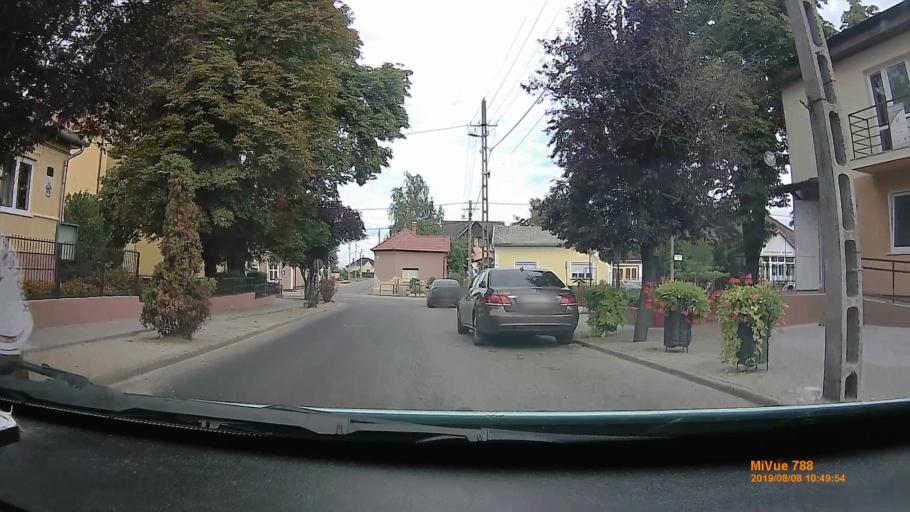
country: HU
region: Szabolcs-Szatmar-Bereg
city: Balkany
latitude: 47.7710
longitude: 21.8626
